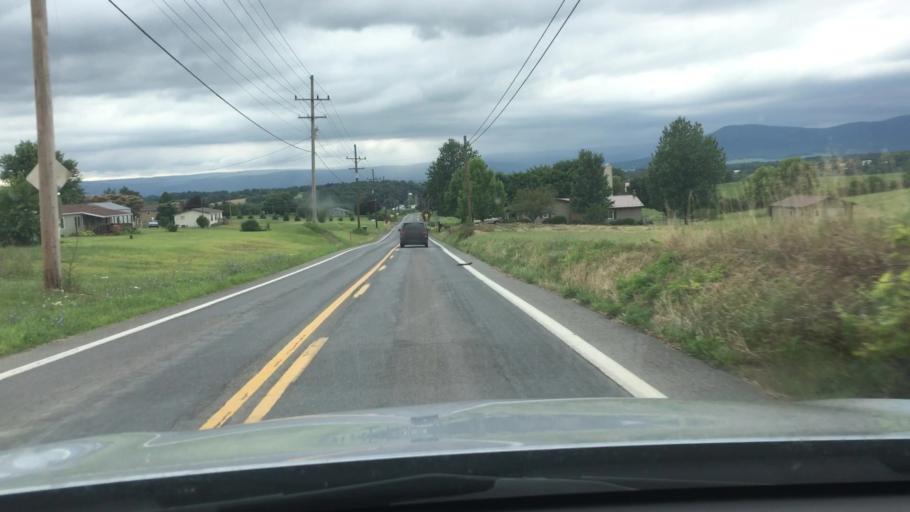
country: US
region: Pennsylvania
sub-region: Franklin County
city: Greencastle
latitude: 39.8647
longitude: -77.7690
